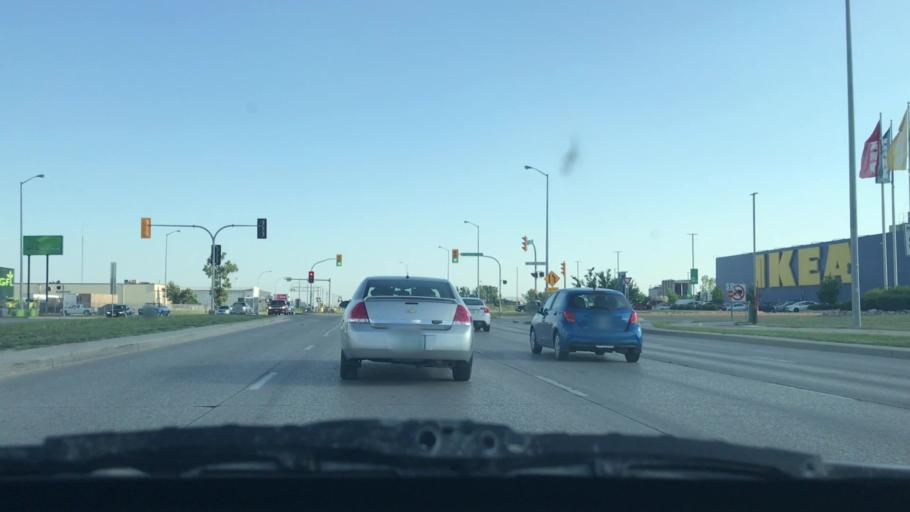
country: CA
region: Manitoba
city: Winnipeg
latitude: 49.8402
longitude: -97.2091
